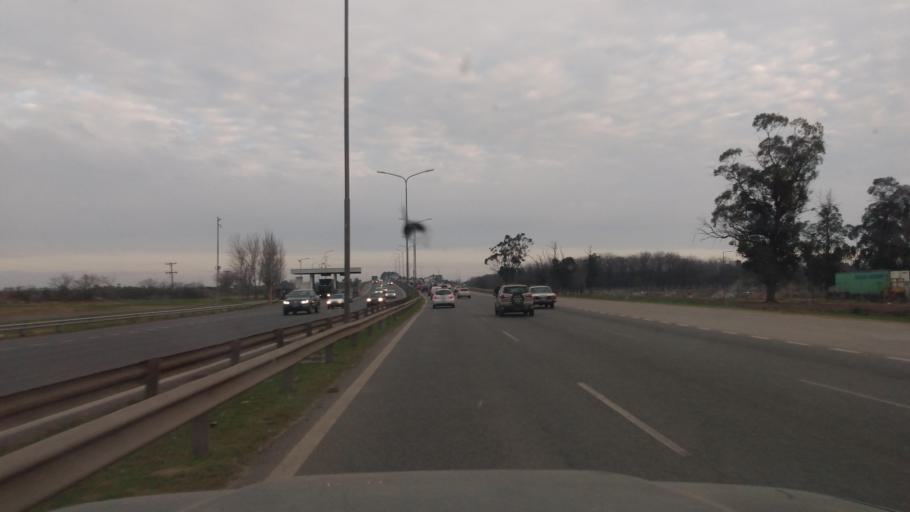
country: AR
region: Buenos Aires
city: Hurlingham
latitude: -34.5587
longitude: -58.6278
